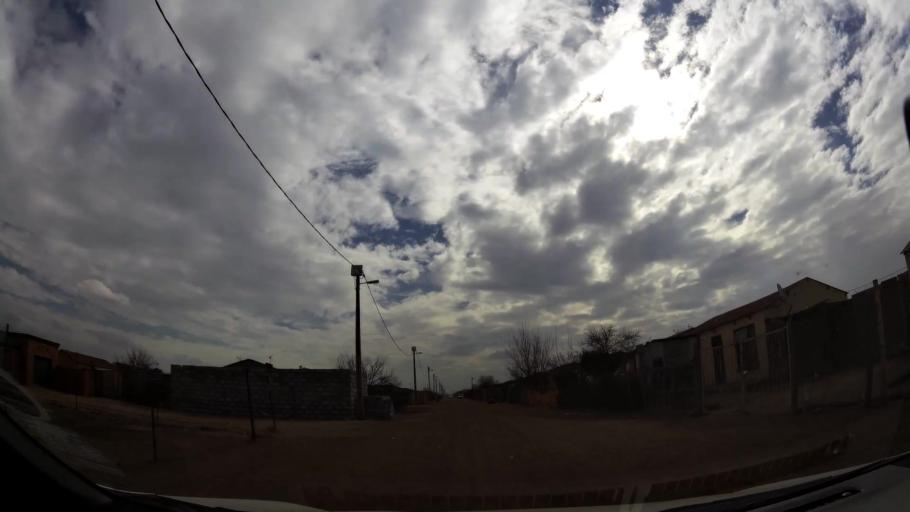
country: ZA
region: Gauteng
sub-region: Ekurhuleni Metropolitan Municipality
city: Germiston
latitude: -26.4140
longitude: 28.1612
